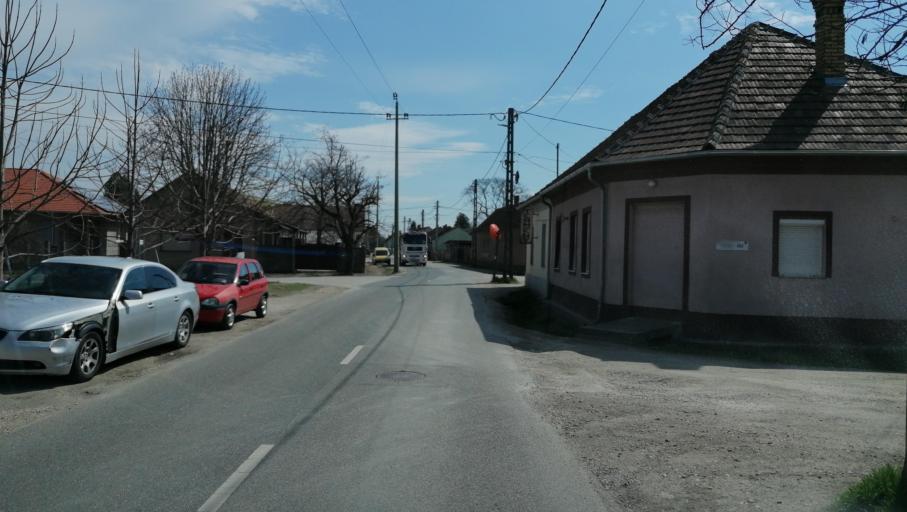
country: HU
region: Pest
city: Kiskunlachaza
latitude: 47.1885
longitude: 19.0022
